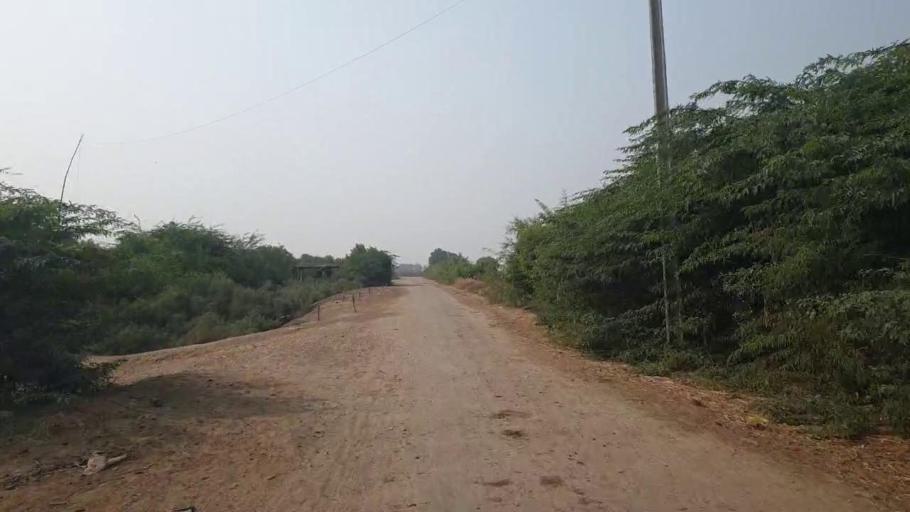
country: PK
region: Sindh
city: Tando Muhammad Khan
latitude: 25.2614
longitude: 68.4652
